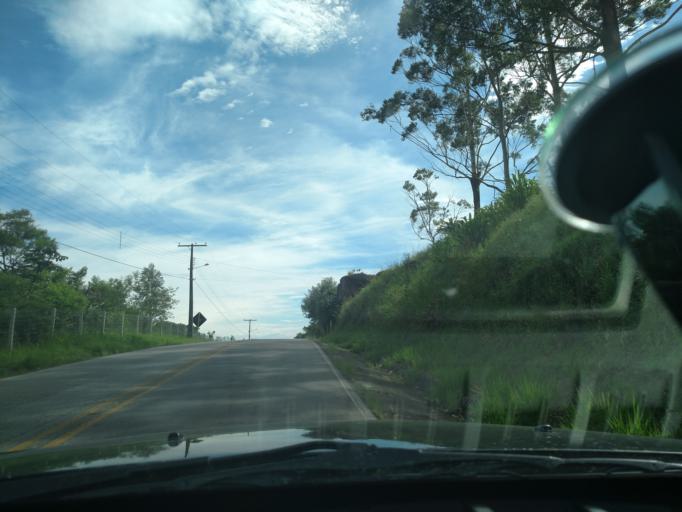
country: BR
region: Santa Catarina
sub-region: Tijucas
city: Tijucas
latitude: -27.3534
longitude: -48.5978
